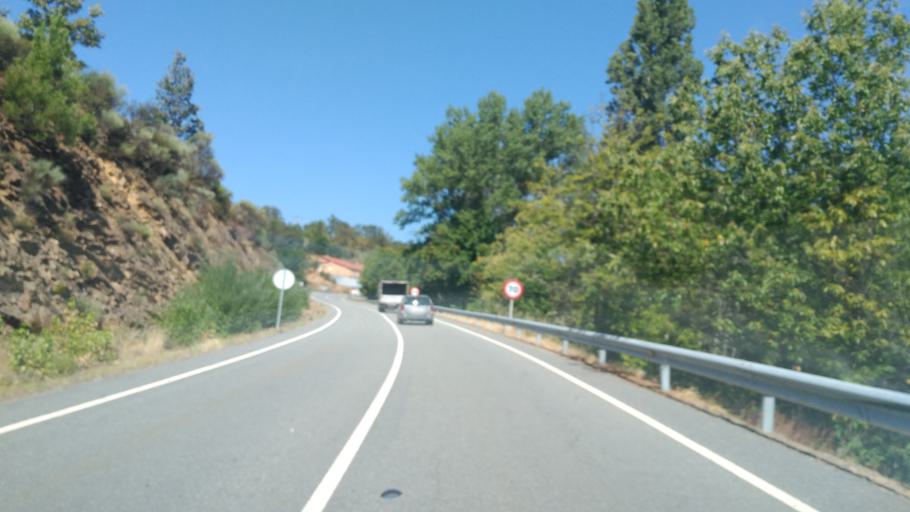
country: ES
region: Castille and Leon
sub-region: Provincia de Salamanca
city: San Martin del Castanar
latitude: 40.5359
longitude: -6.0456
